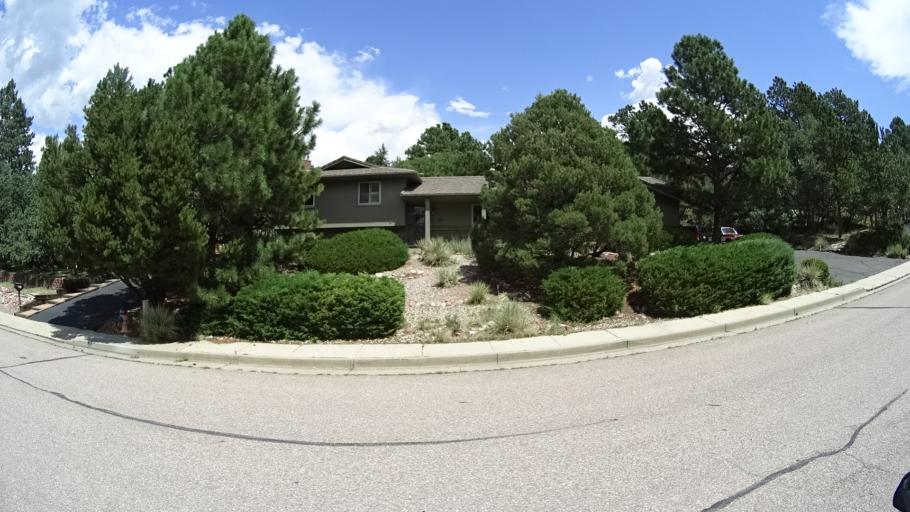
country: US
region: Colorado
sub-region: El Paso County
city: Air Force Academy
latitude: 38.9342
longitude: -104.8287
